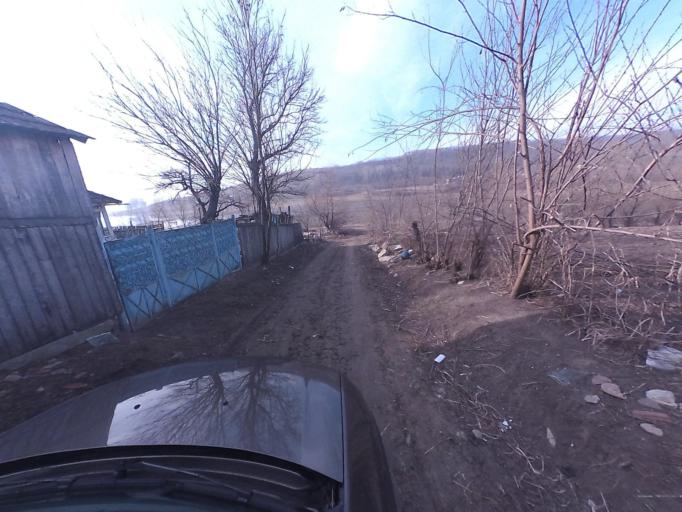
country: RO
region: Vaslui
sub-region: Comuna Solesti
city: Solesti
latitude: 46.8046
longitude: 27.7847
